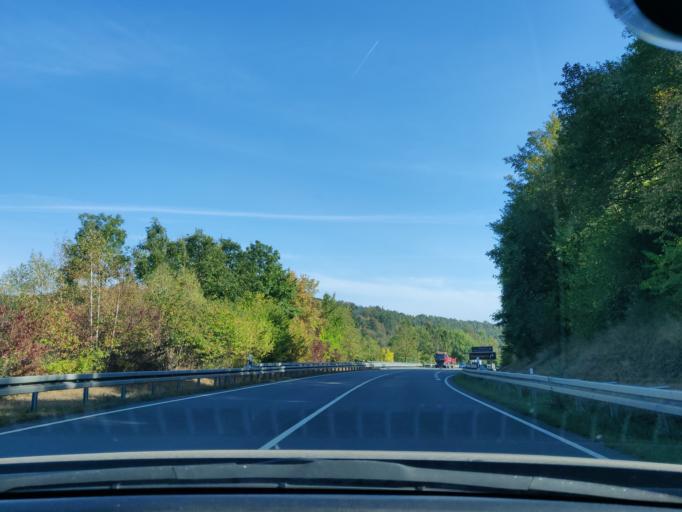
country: DE
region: Hesse
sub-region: Regierungsbezirk Kassel
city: Bad Wildungen
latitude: 51.1233
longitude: 9.1577
